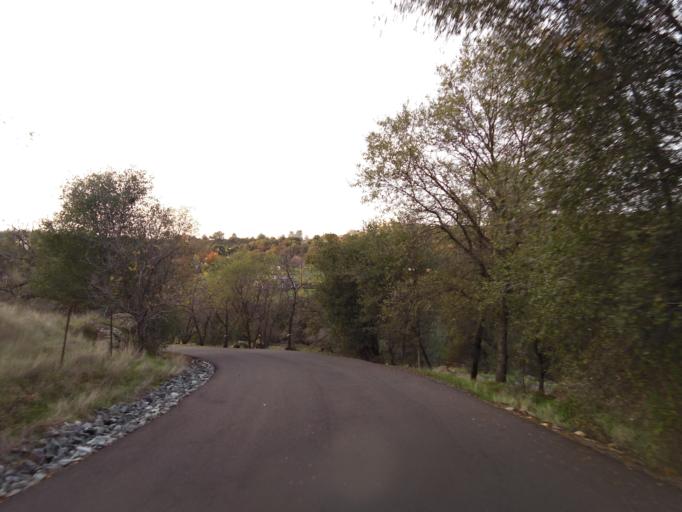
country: US
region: California
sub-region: El Dorado County
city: Cameron Park
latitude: 38.7421
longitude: -120.9918
